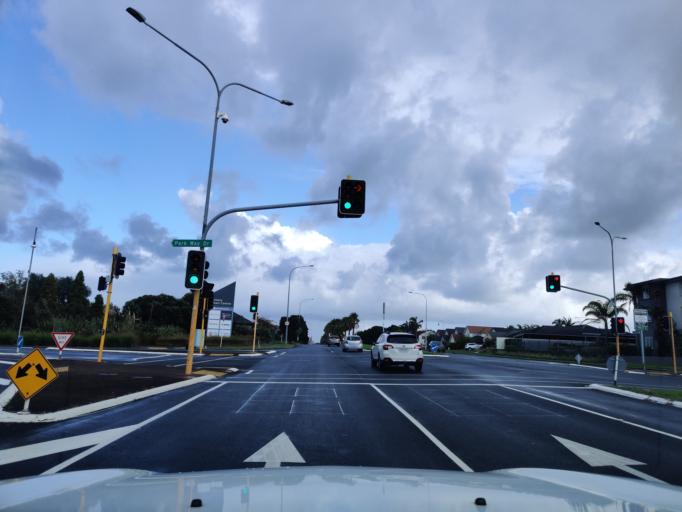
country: NZ
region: Auckland
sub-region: Auckland
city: Pakuranga
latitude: -36.9342
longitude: 174.9104
